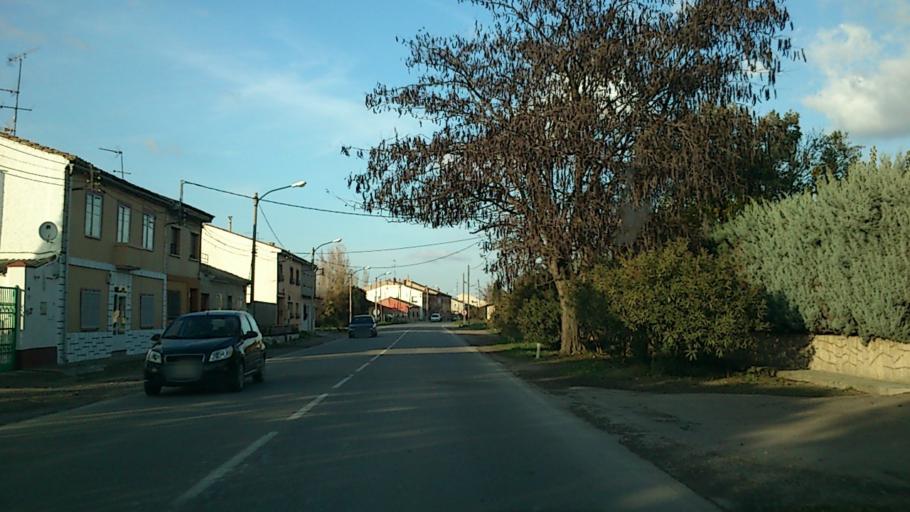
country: ES
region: Aragon
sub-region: Provincia de Zaragoza
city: Villanueva de Gallego
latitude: 41.7005
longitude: -0.8152
